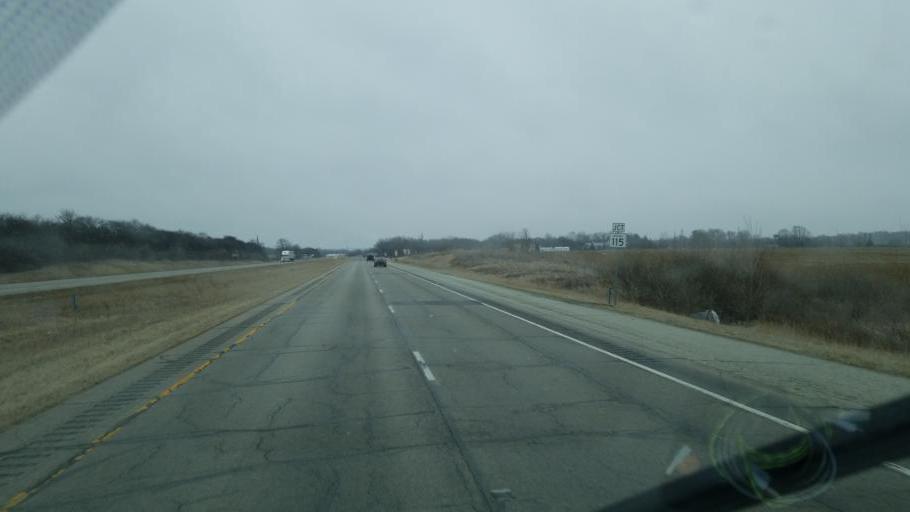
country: US
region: Indiana
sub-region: Wabash County
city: Wabash
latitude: 40.8001
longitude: -85.8737
